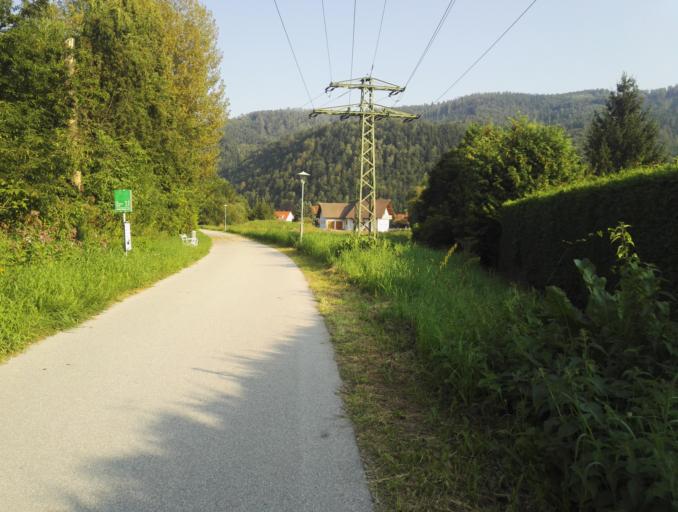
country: AT
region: Styria
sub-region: Politischer Bezirk Graz-Umgebung
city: Gratkorn
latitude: 47.1210
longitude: 15.3491
